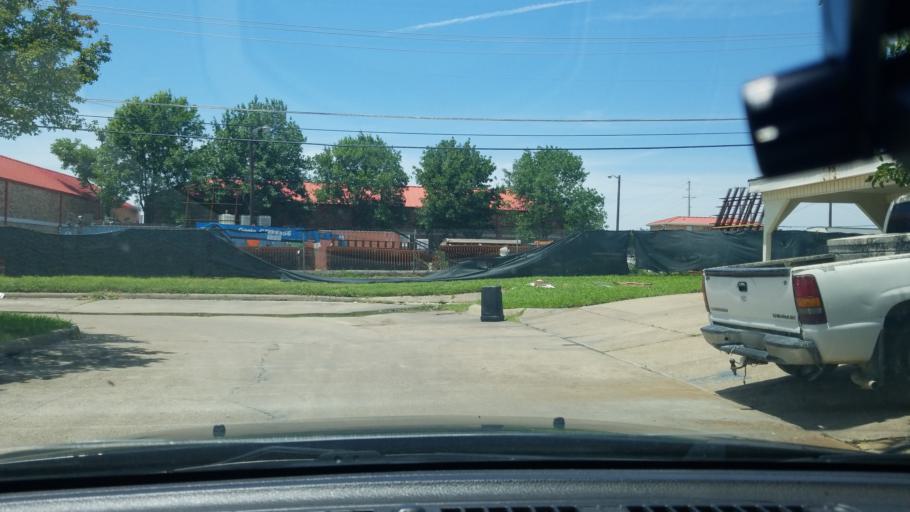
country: US
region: Texas
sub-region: Dallas County
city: Mesquite
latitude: 32.7908
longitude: -96.6119
